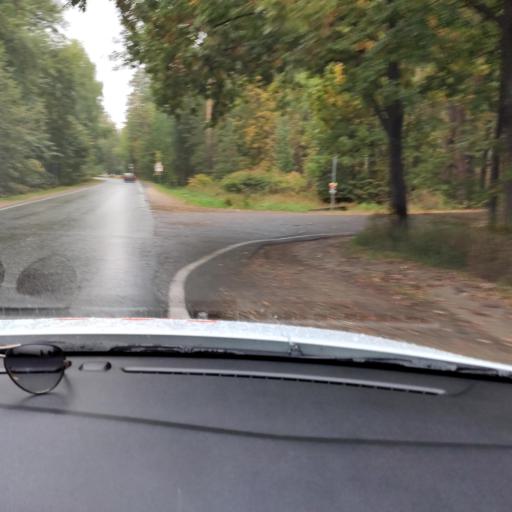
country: RU
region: Tatarstan
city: Verkhniy Uslon
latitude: 55.6401
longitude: 49.0229
